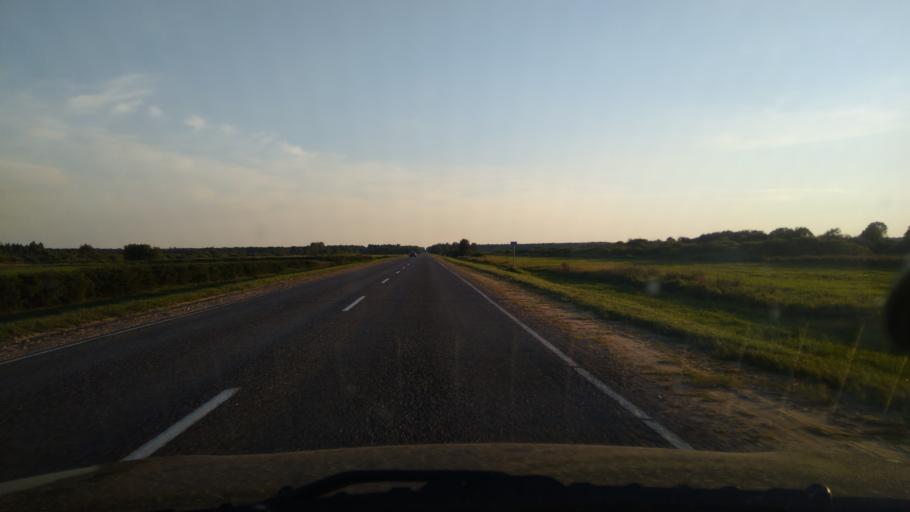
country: BY
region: Brest
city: Nyakhachava
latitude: 52.6253
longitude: 25.1677
